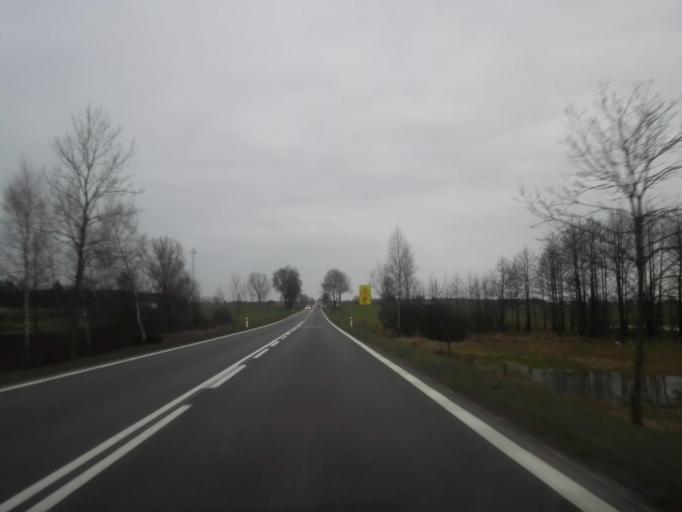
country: PL
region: Podlasie
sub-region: Powiat kolnenski
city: Stawiski
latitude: 53.4698
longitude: 22.2043
